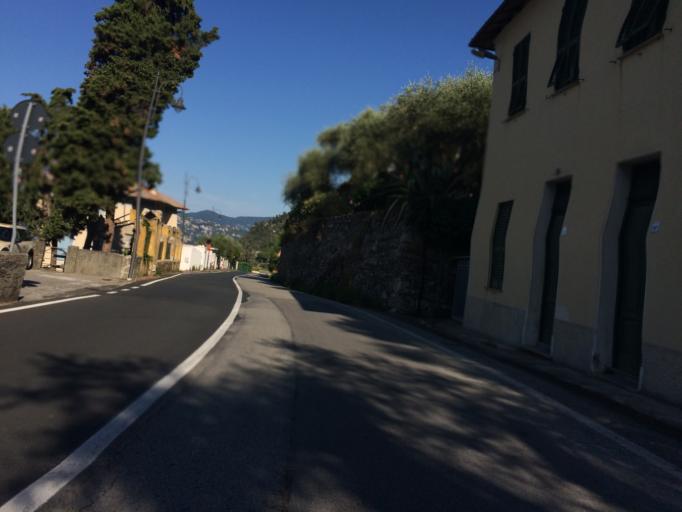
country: IT
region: Liguria
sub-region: Provincia di Genova
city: Zoagli
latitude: 44.3341
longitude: 9.2738
